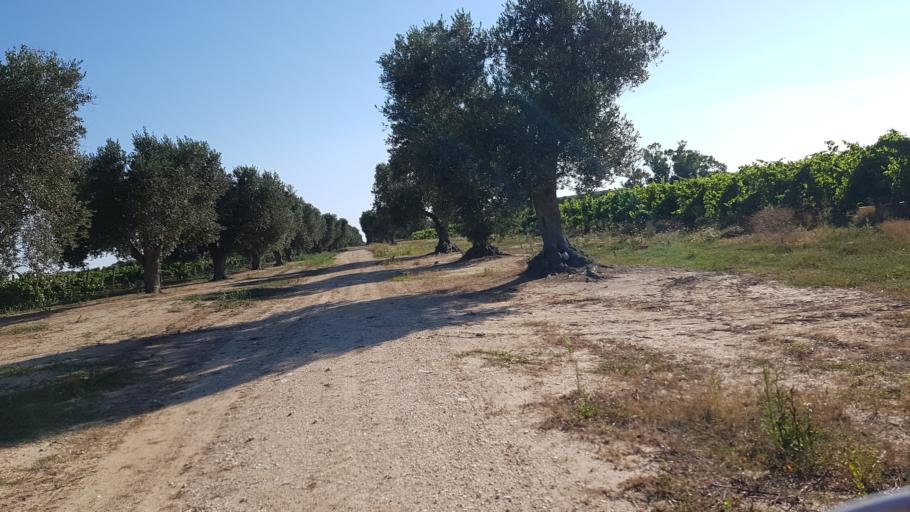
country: IT
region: Apulia
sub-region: Provincia di Brindisi
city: La Rosa
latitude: 40.5901
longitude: 17.9926
